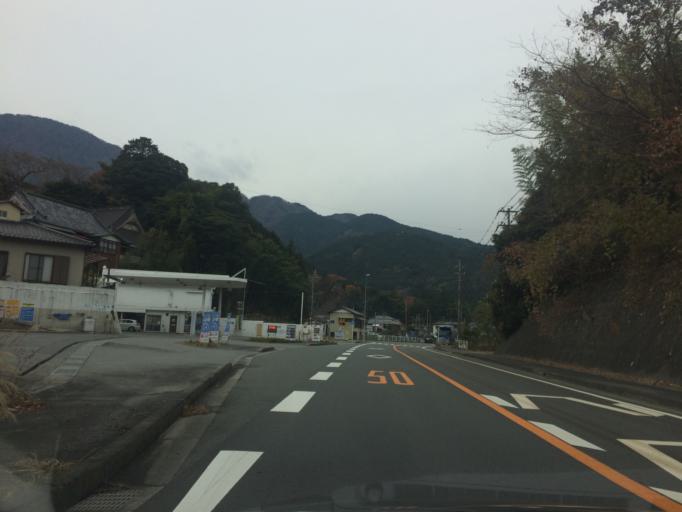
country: JP
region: Shizuoka
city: Fujinomiya
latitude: 35.2623
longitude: 138.4682
